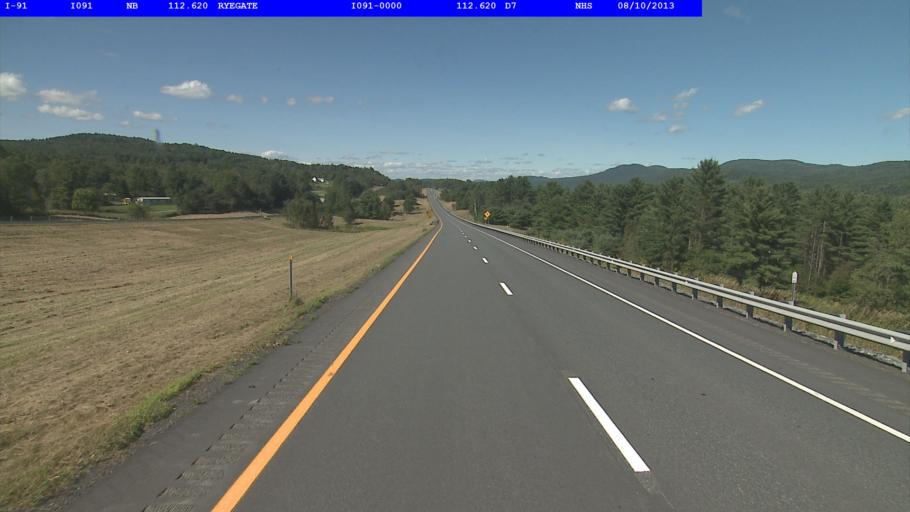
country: US
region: New Hampshire
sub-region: Grafton County
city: Woodsville
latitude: 44.1909
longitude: -72.0734
